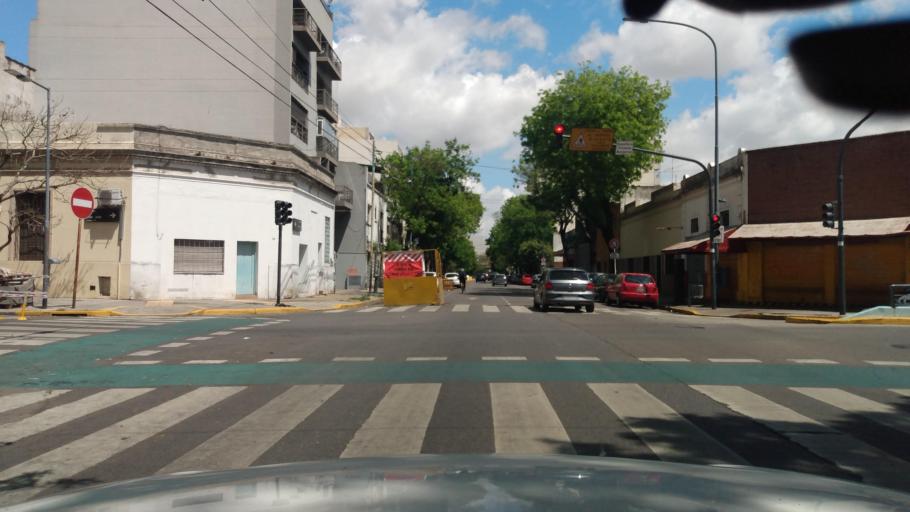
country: AR
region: Buenos Aires
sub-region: Partido de General San Martin
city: General San Martin
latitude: -34.5781
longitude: -58.4929
